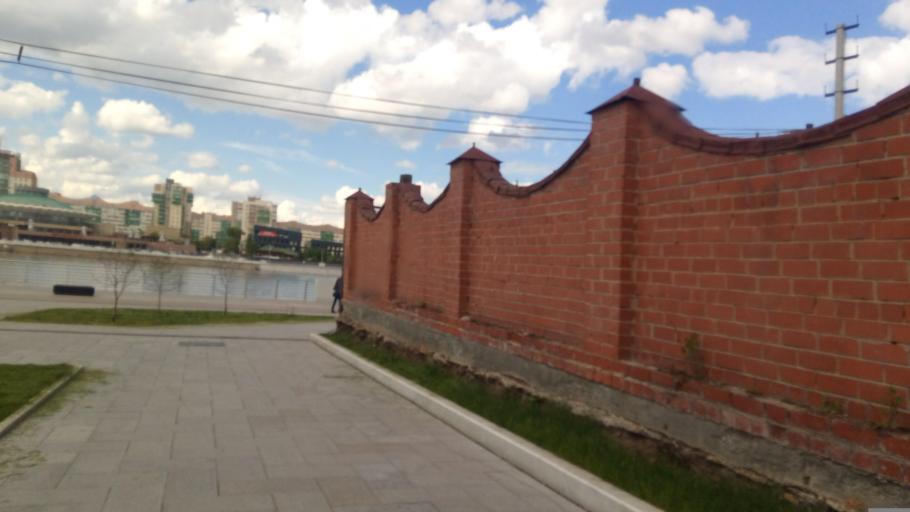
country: RU
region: Chelyabinsk
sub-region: Gorod Chelyabinsk
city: Chelyabinsk
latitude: 55.1684
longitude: 61.4034
